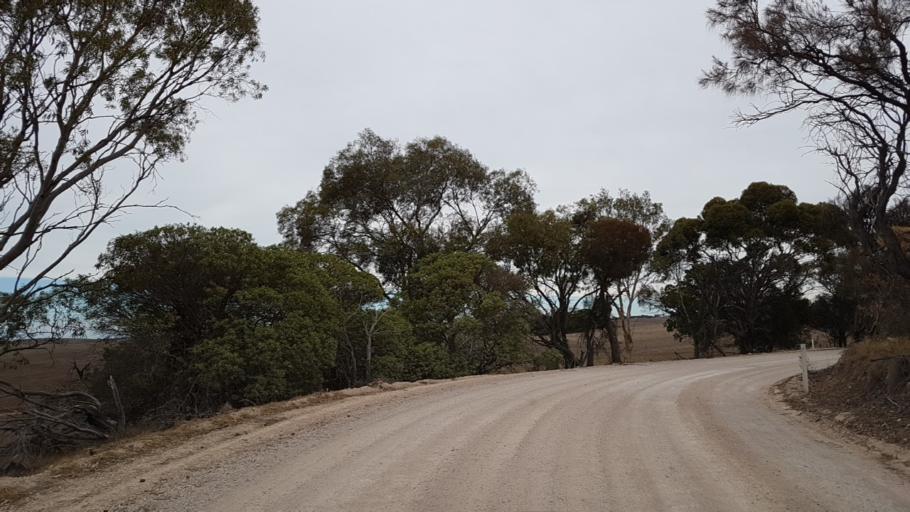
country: AU
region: South Australia
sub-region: Mount Barker
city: Nairne
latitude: -35.0018
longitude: 139.0062
